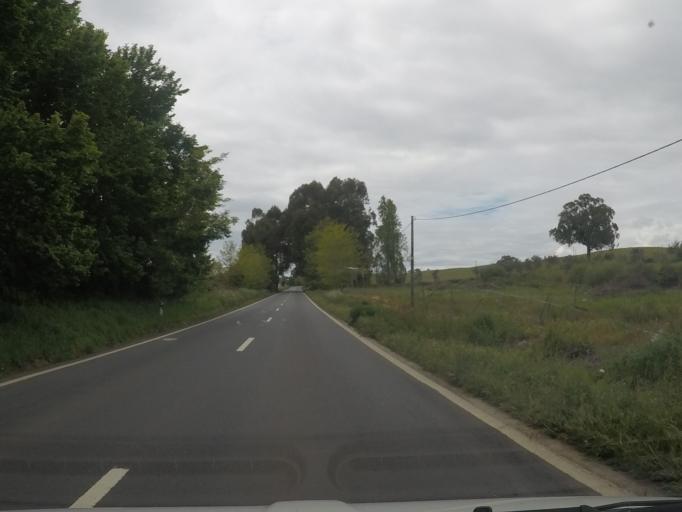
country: PT
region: Setubal
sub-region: Santiago do Cacem
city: Cercal
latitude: 37.8223
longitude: -8.6881
